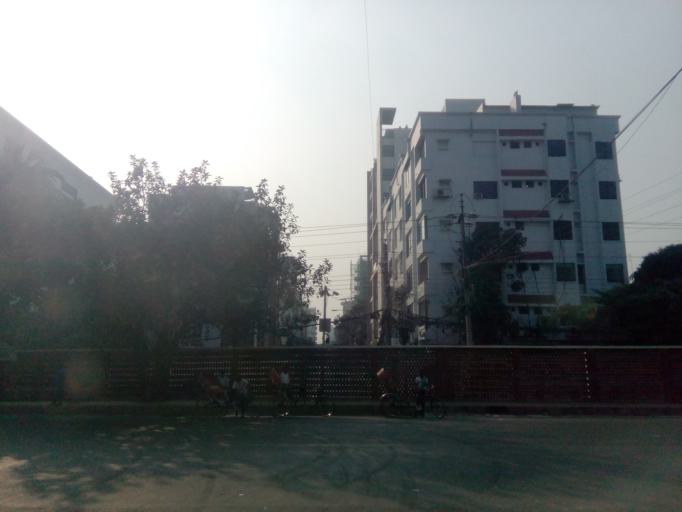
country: BD
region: Dhaka
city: Paltan
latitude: 23.8048
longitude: 90.4216
